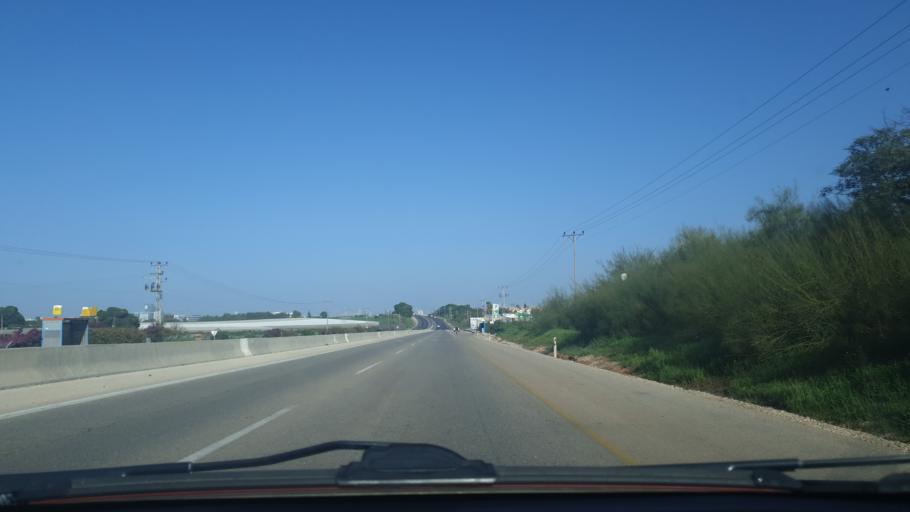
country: IL
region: Central District
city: Bet Dagan
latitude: 31.9873
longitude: 34.8310
